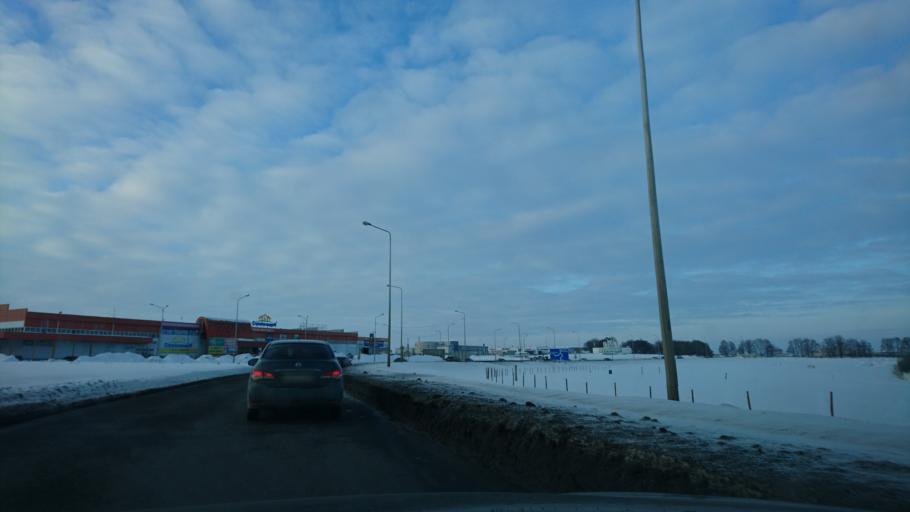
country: RU
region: Belgorod
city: Severnyy
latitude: 50.6578
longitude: 36.5651
